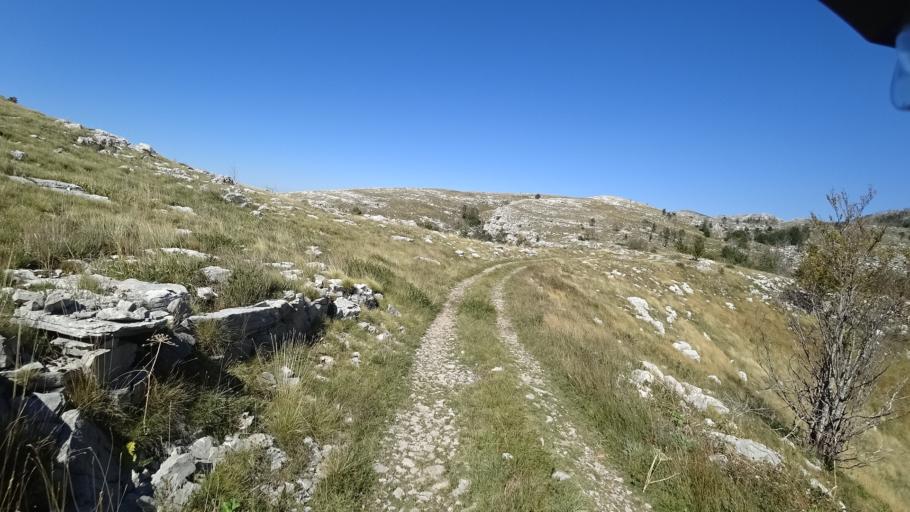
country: HR
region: Splitsko-Dalmatinska
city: Hrvace
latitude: 43.9098
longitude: 16.6126
